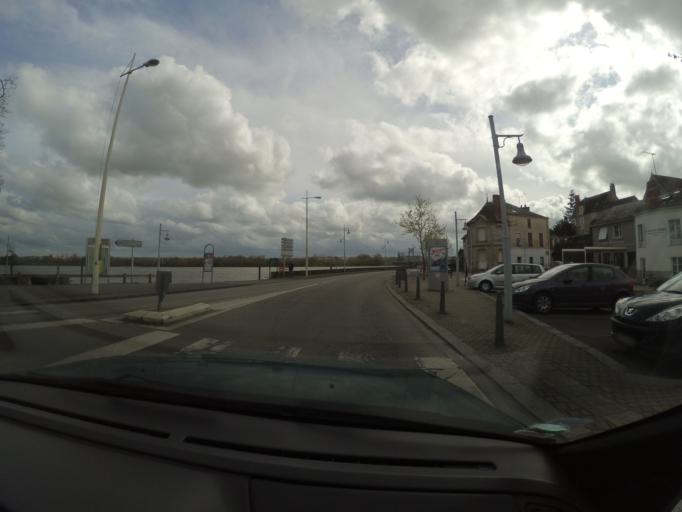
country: FR
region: Pays de la Loire
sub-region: Departement de la Loire-Atlantique
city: Ancenis
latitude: 47.3666
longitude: -1.1744
